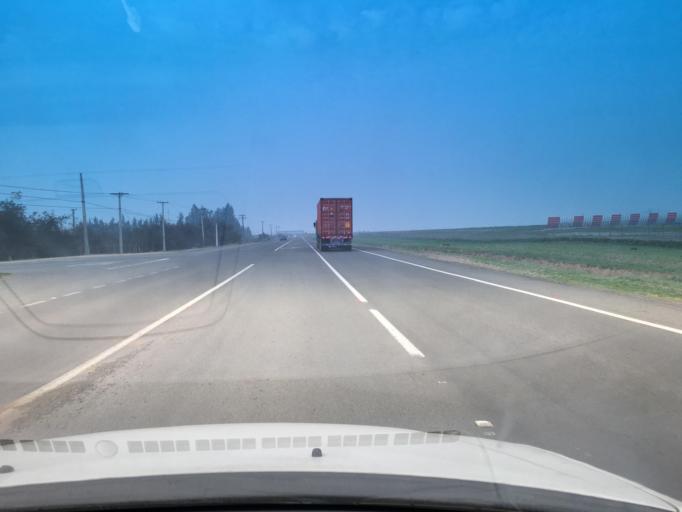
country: CL
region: Santiago Metropolitan
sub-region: Provincia de Santiago
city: Lo Prado
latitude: -33.3785
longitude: -70.7986
